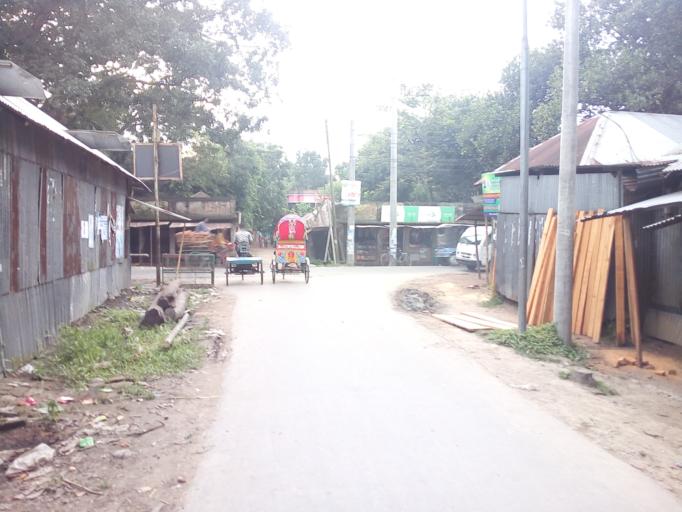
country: BD
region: Khulna
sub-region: Magura
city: Magura
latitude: 23.5494
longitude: 89.6262
